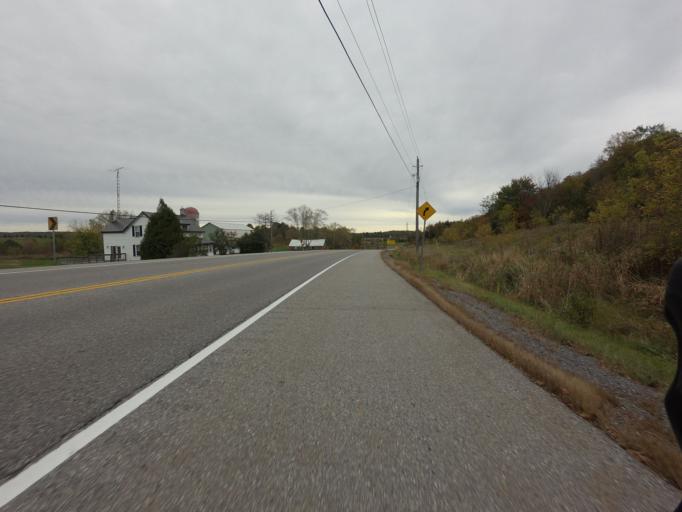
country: CA
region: Ontario
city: Gananoque
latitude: 44.4573
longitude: -76.2667
